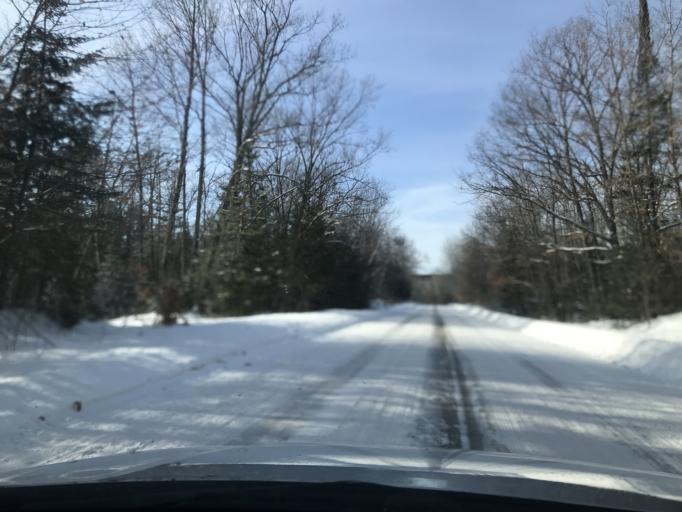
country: US
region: Wisconsin
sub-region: Oconto County
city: Gillett
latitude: 45.1573
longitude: -88.2061
